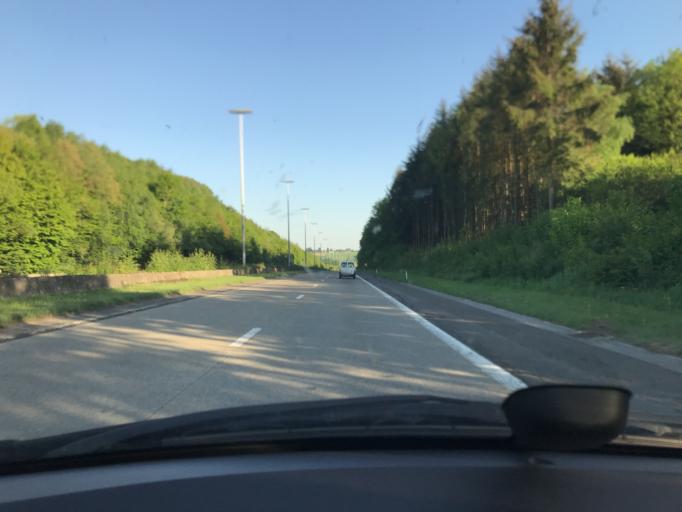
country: BE
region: Wallonia
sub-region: Province de Namur
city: Assesse
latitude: 50.3736
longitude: 4.9938
